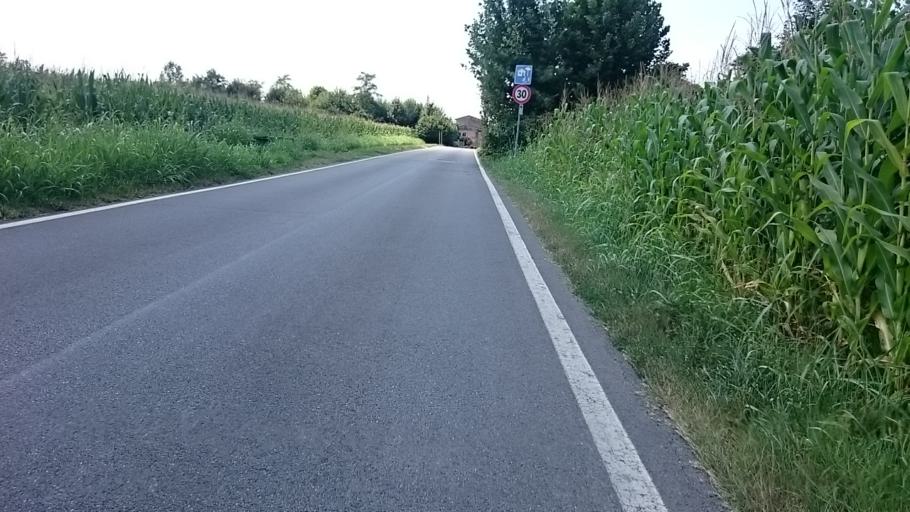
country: IT
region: Veneto
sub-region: Provincia di Vicenza
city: Rosa
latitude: 45.7056
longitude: 11.7414
